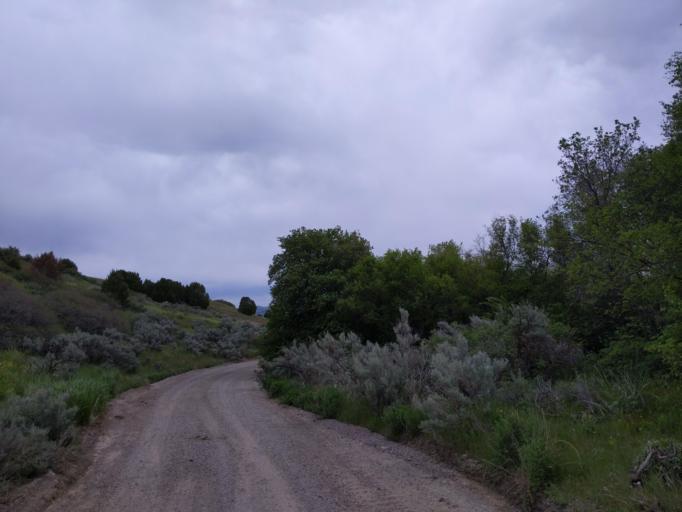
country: US
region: Idaho
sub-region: Bannock County
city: Pocatello
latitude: 42.8395
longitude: -112.4646
